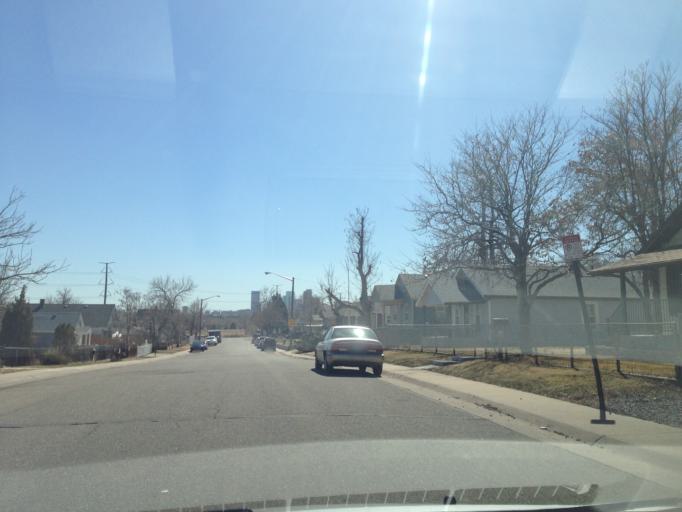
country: US
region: Colorado
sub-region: Adams County
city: Twin Lakes
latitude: 39.7892
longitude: -104.9840
